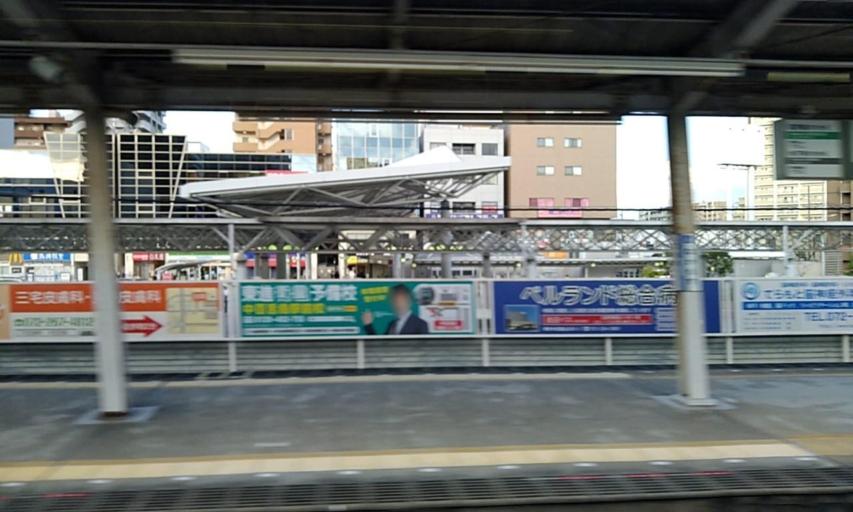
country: JP
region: Osaka
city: Matsubara
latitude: 34.5559
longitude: 135.5050
